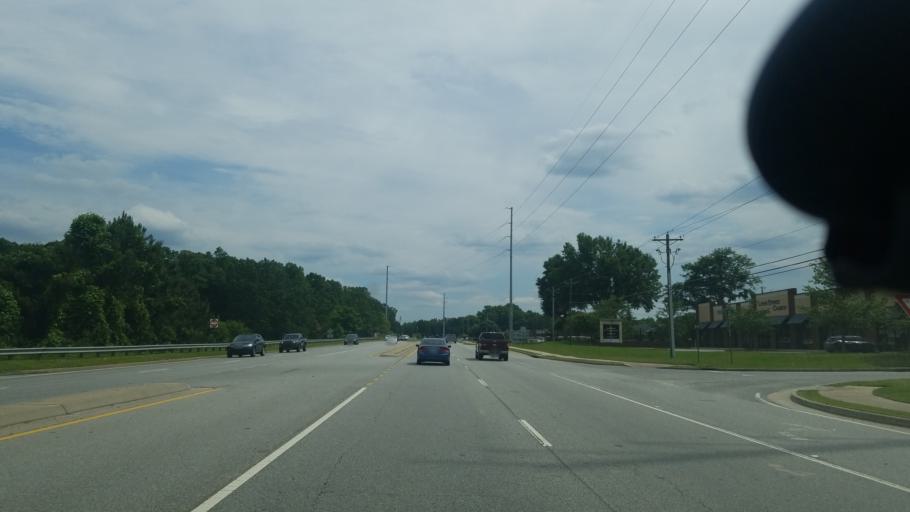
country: US
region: Georgia
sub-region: Forsyth County
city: Cumming
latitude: 34.1610
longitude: -84.1531
